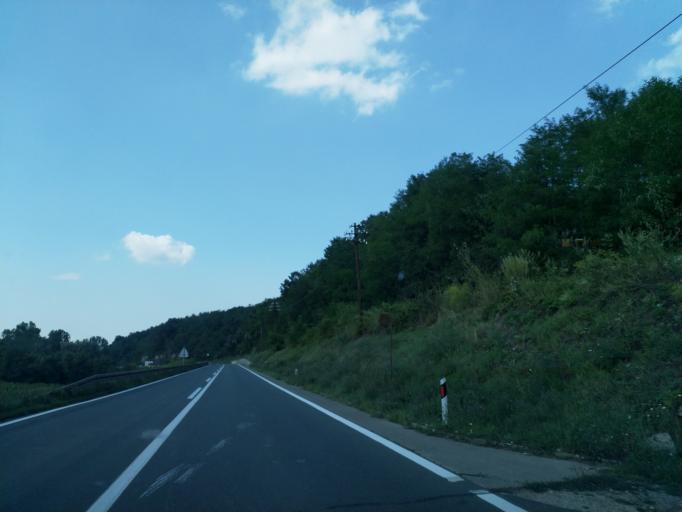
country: RS
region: Central Serbia
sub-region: Rasinski Okrug
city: Krusevac
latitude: 43.6445
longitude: 21.3828
